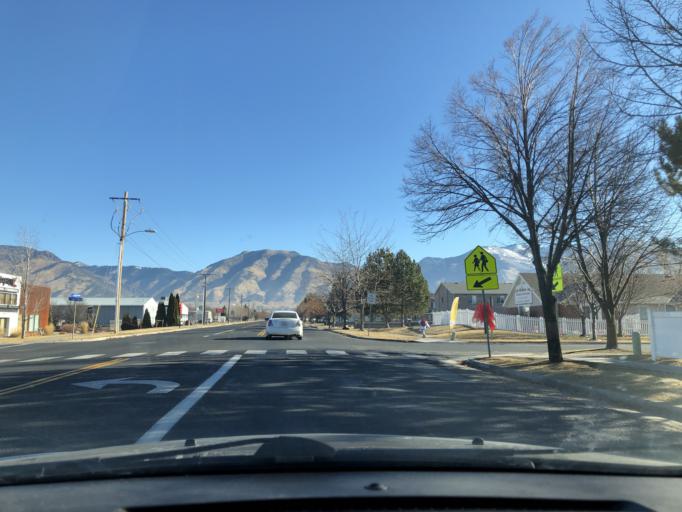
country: US
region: Utah
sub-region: Cache County
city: Logan
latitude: 41.7578
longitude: -111.8445
